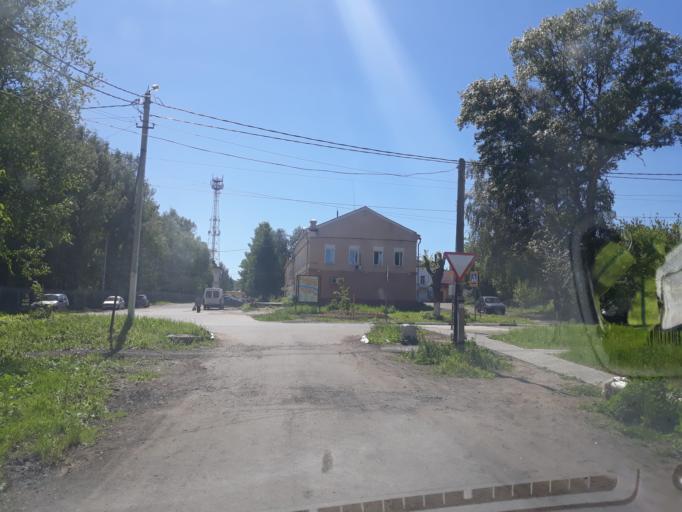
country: RU
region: Jaroslavl
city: Tutayev
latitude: 57.8710
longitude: 39.5311
